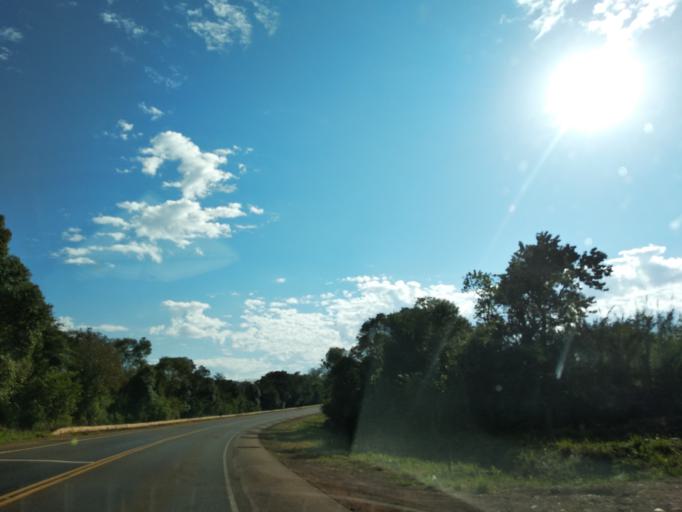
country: AR
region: Misiones
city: Aristobulo del Valle
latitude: -27.1026
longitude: -54.9671
